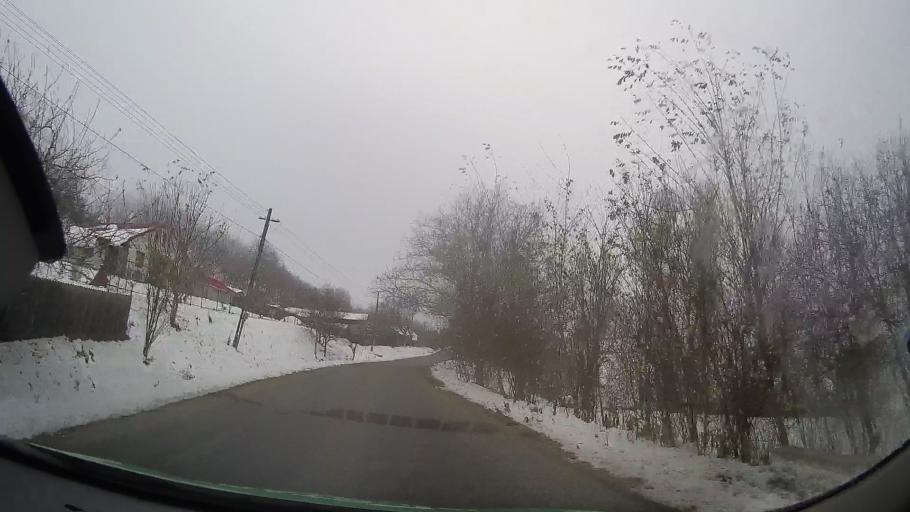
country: RO
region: Bacau
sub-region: Comuna Vultureni
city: Vultureni
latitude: 46.3882
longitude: 27.2787
